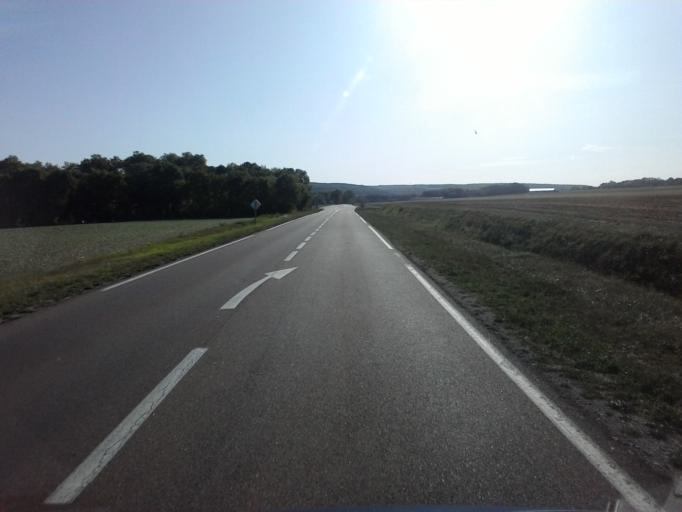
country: FR
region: Champagne-Ardenne
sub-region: Departement de l'Aube
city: Bar-sur-Seine
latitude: 48.1267
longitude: 4.3555
